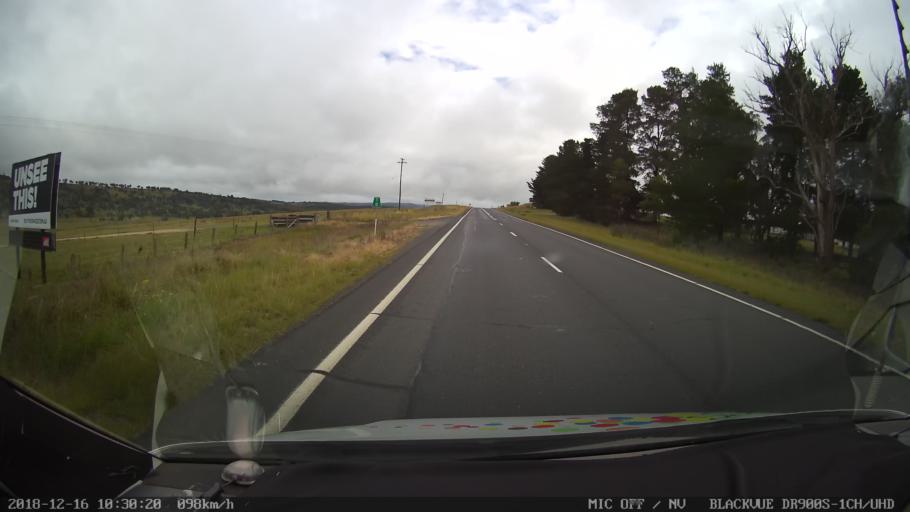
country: AU
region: New South Wales
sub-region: Tenterfield Municipality
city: Carrolls Creek
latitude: -29.0948
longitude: 152.0023
